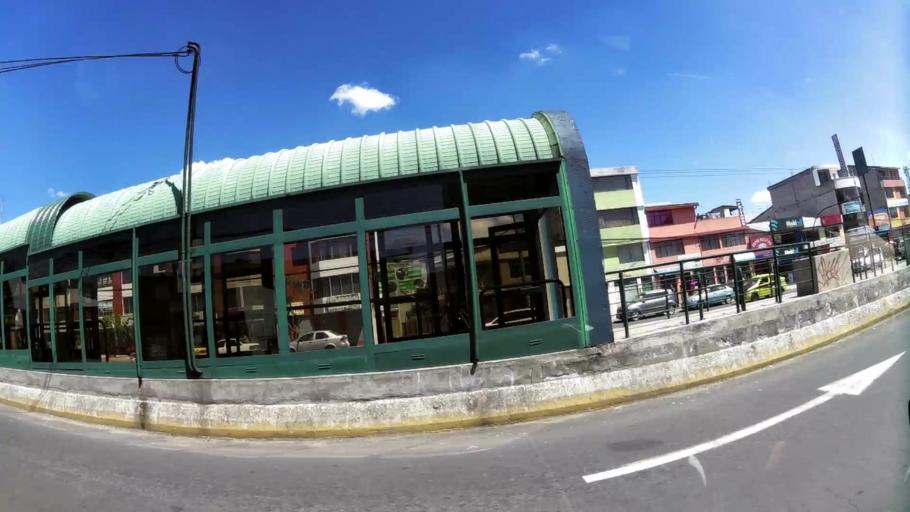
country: EC
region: Pichincha
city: Quito
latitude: -0.1243
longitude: -78.4938
